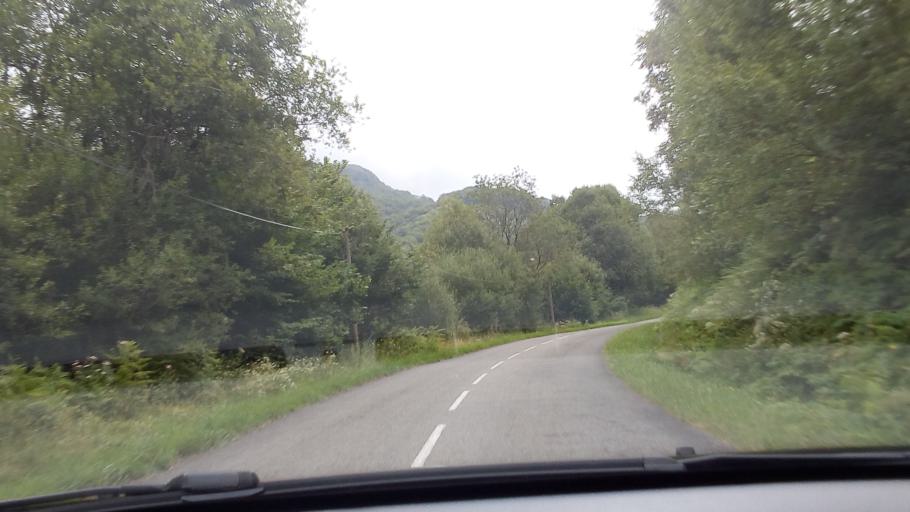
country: FR
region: Aquitaine
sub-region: Departement des Pyrenees-Atlantiques
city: Ogeu-les-Bains
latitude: 43.0733
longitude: -0.5364
